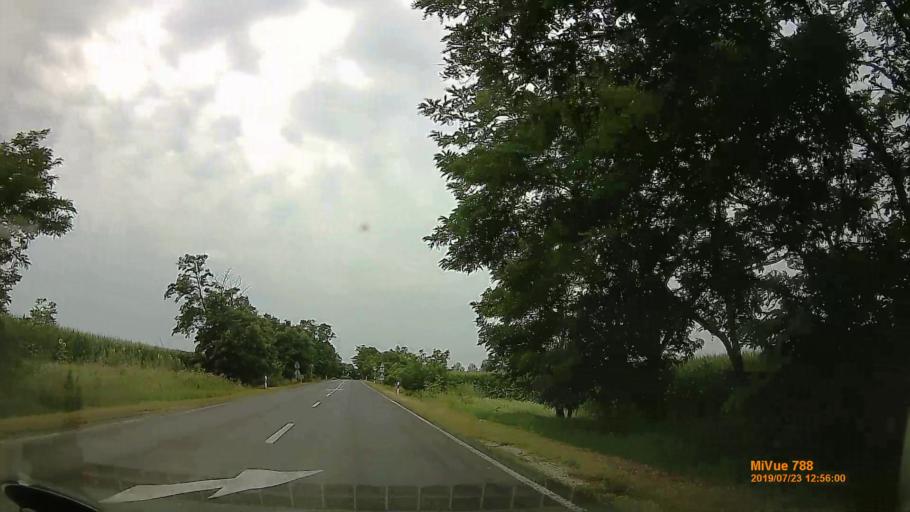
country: HU
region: Szabolcs-Szatmar-Bereg
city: Nagycserkesz
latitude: 47.9576
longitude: 21.5075
